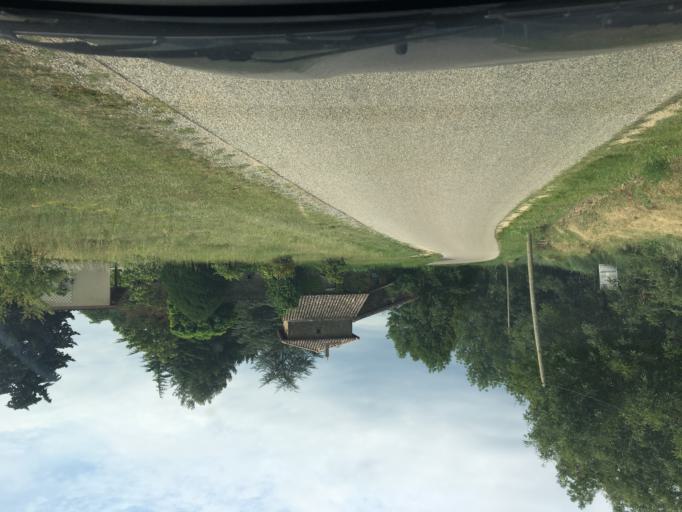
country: FR
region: Rhone-Alpes
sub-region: Departement de la Drome
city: Clerieux
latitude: 45.1275
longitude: 4.9454
